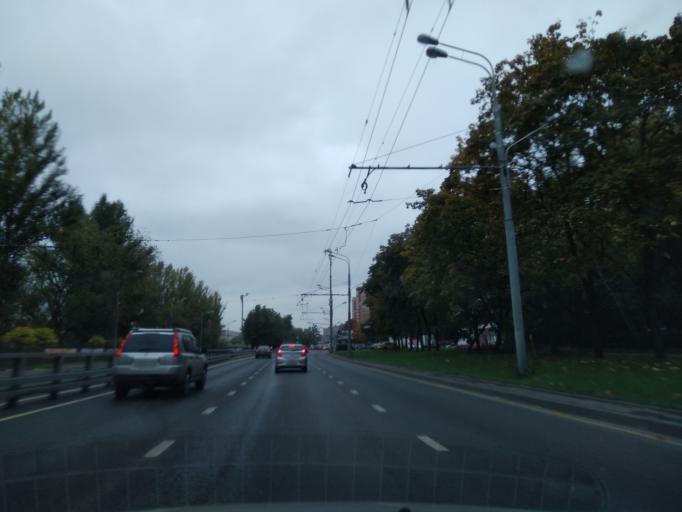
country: RU
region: Moscow
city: Likhobory
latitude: 55.8431
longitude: 37.5560
